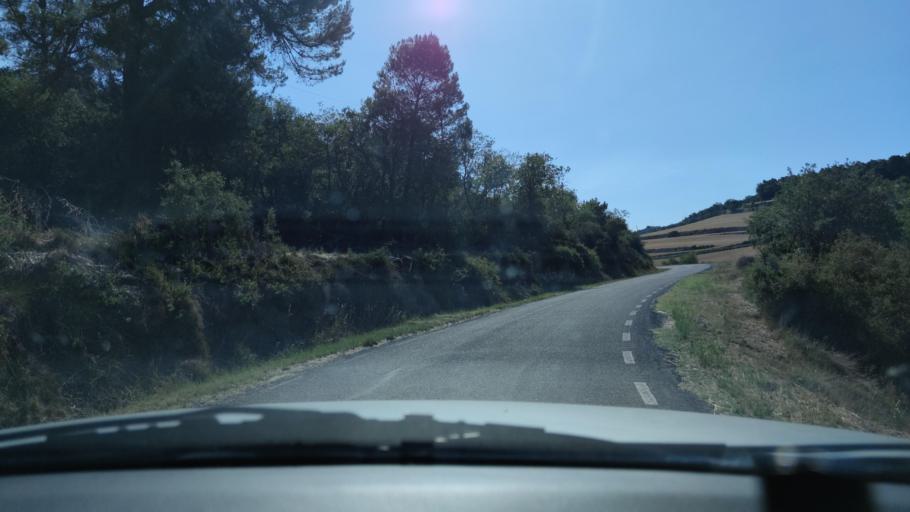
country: ES
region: Catalonia
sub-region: Provincia de Barcelona
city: Pujalt
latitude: 41.7097
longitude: 1.3756
